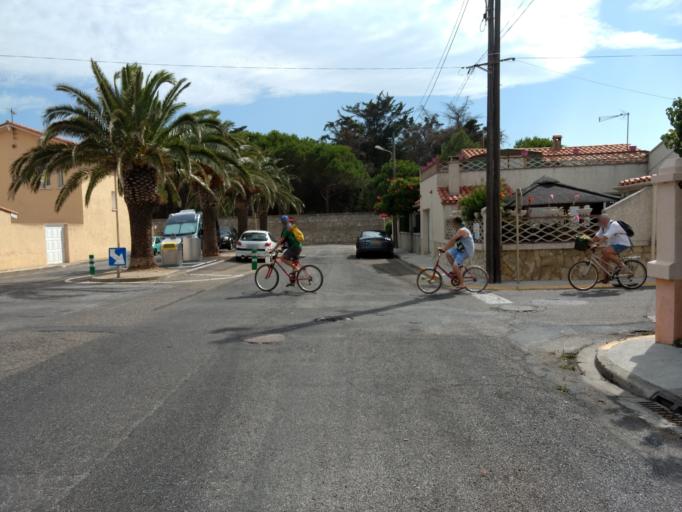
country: FR
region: Languedoc-Roussillon
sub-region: Departement des Pyrenees-Orientales
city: Le Barcares
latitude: 42.7859
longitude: 3.0349
